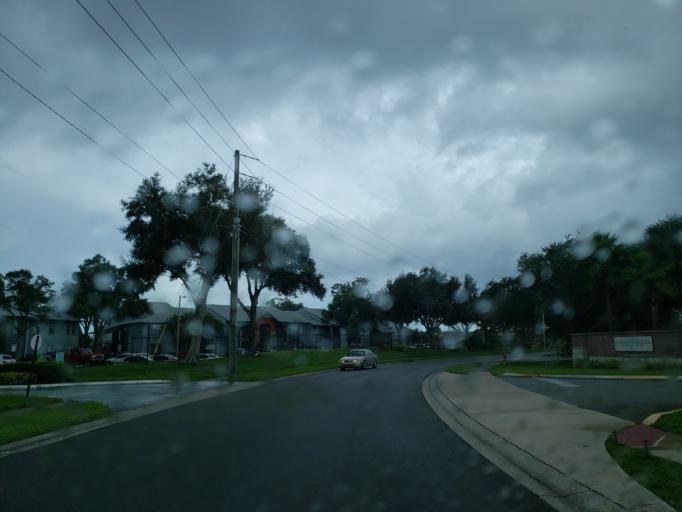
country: US
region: Florida
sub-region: Hillsborough County
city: Brandon
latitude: 27.9250
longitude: -82.3211
